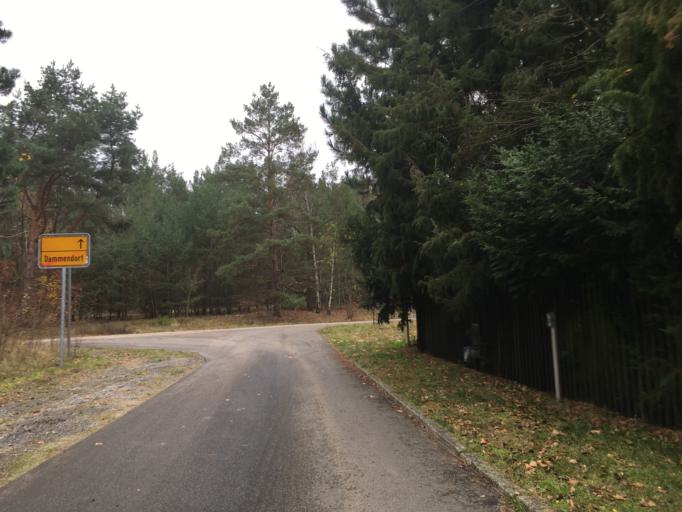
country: DE
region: Brandenburg
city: Mixdorf
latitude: 52.1471
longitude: 14.4181
